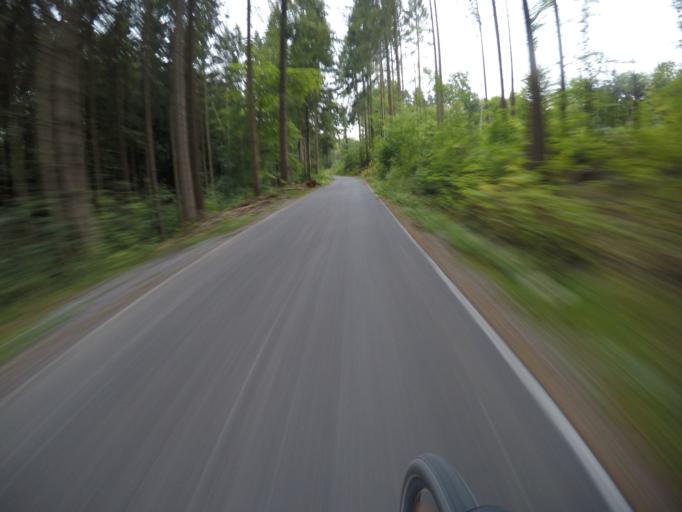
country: DE
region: Baden-Wuerttemberg
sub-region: Regierungsbezirk Stuttgart
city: Steinenbronn
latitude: 48.7088
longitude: 9.0927
